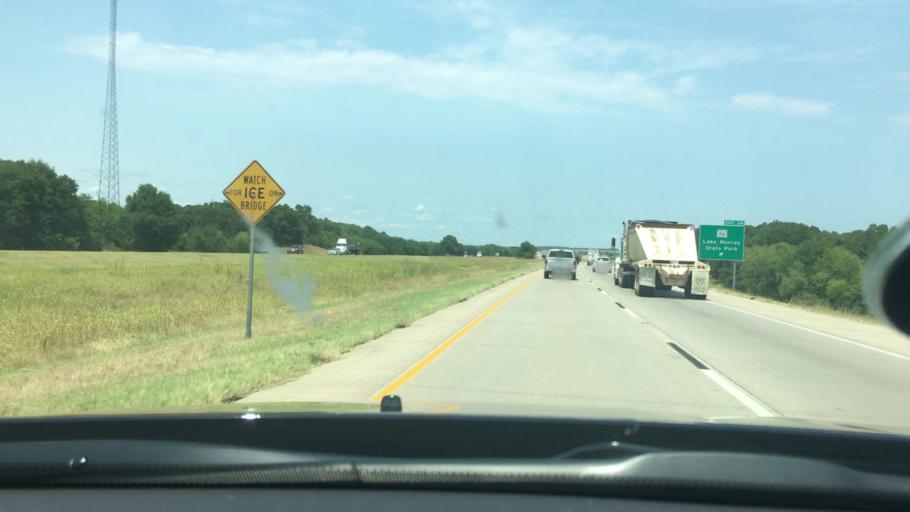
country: US
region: Oklahoma
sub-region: Carter County
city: Ardmore
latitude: 34.0651
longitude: -97.1496
